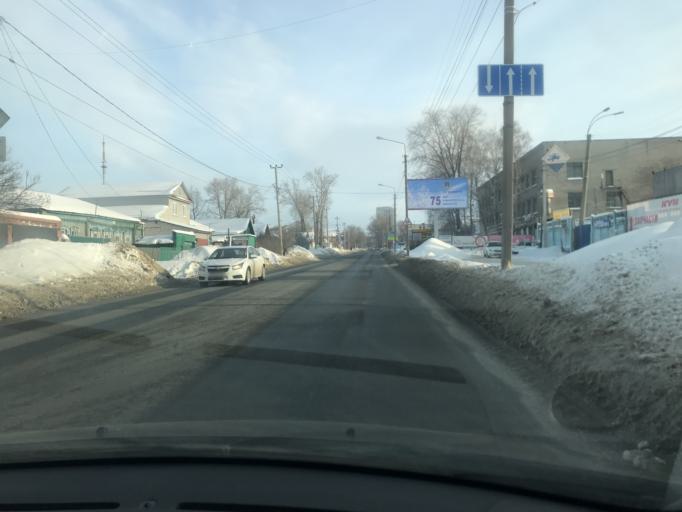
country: RU
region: Ulyanovsk
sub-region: Ulyanovskiy Rayon
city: Ulyanovsk
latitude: 54.3335
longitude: 48.3711
